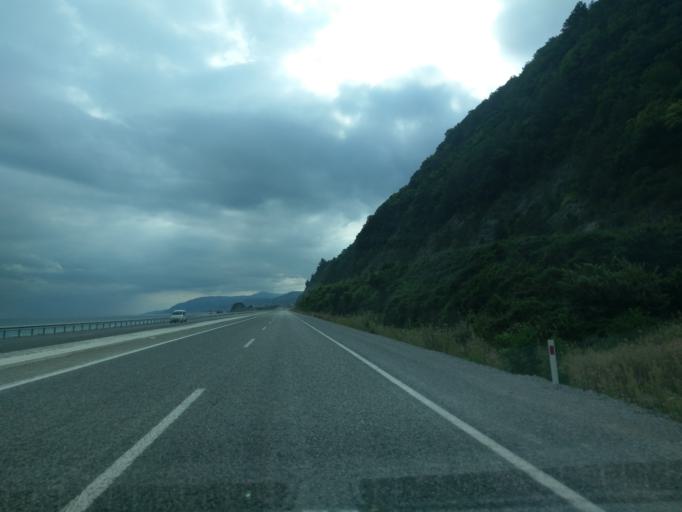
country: TR
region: Kastamonu
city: Catalzeytin
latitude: 41.9474
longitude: 34.2641
